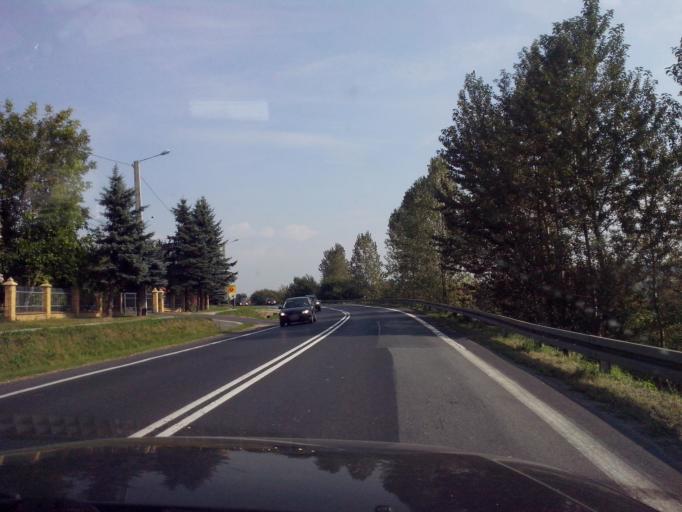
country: PL
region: Subcarpathian Voivodeship
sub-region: Powiat rzeszowski
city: Lubenia
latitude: 49.9362
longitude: 21.9031
